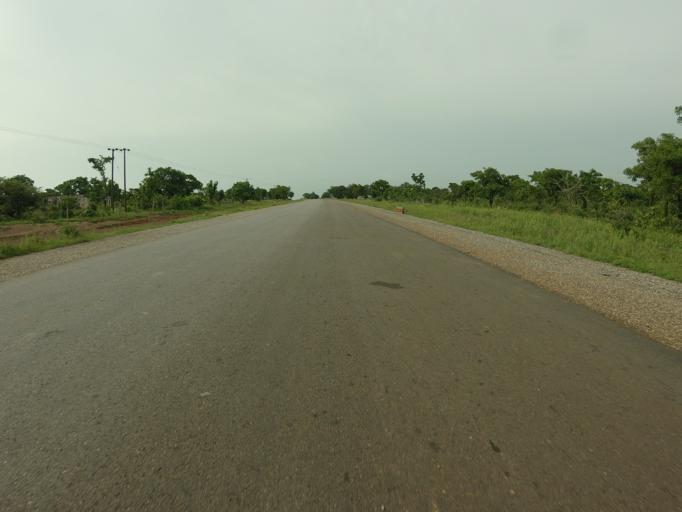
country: GH
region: Northern
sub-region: Yendi
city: Yendi
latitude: 9.6435
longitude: -0.0668
